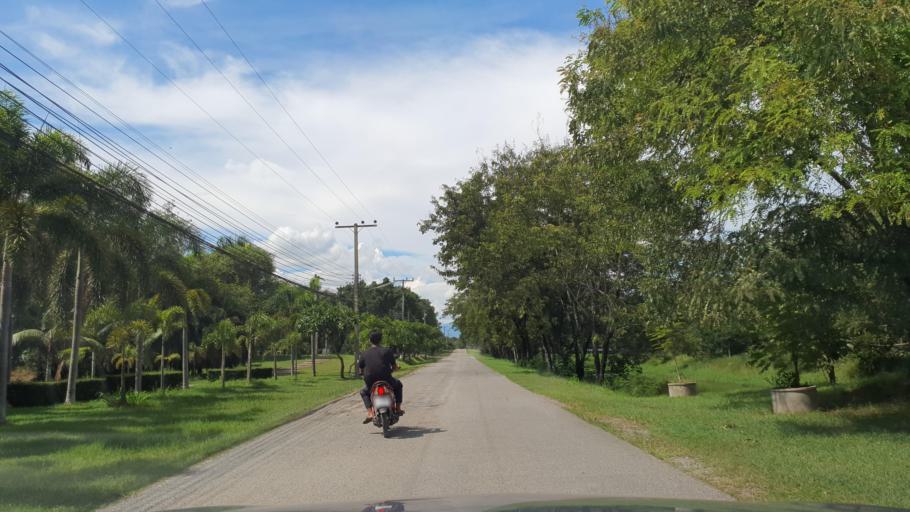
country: TH
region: Chiang Mai
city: San Pa Tong
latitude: 18.5832
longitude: 98.8741
